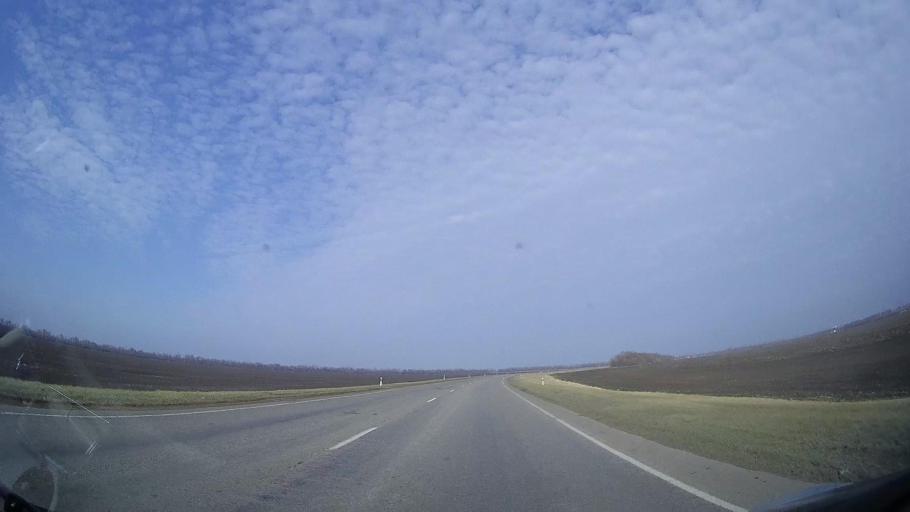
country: RU
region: Rostov
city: Tselina
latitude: 46.5165
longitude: 40.9958
